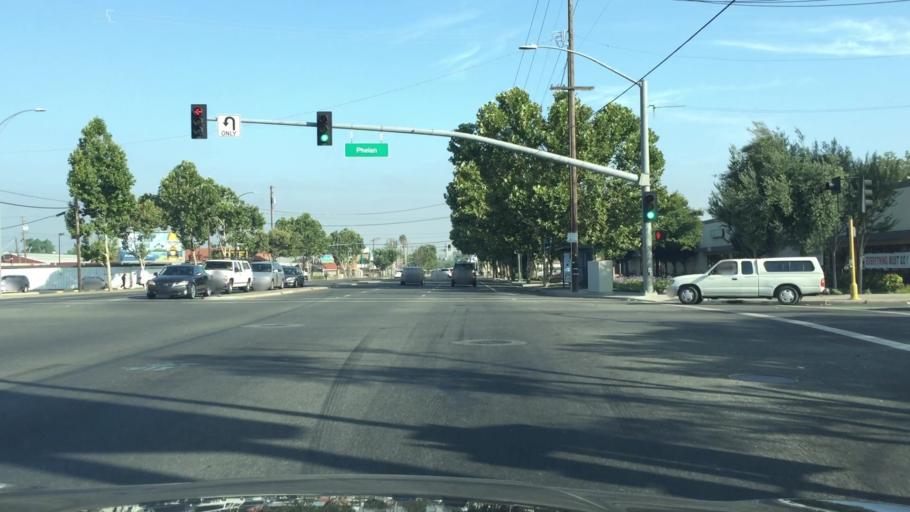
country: US
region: California
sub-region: Santa Clara County
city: San Jose
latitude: 37.3114
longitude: -121.8687
